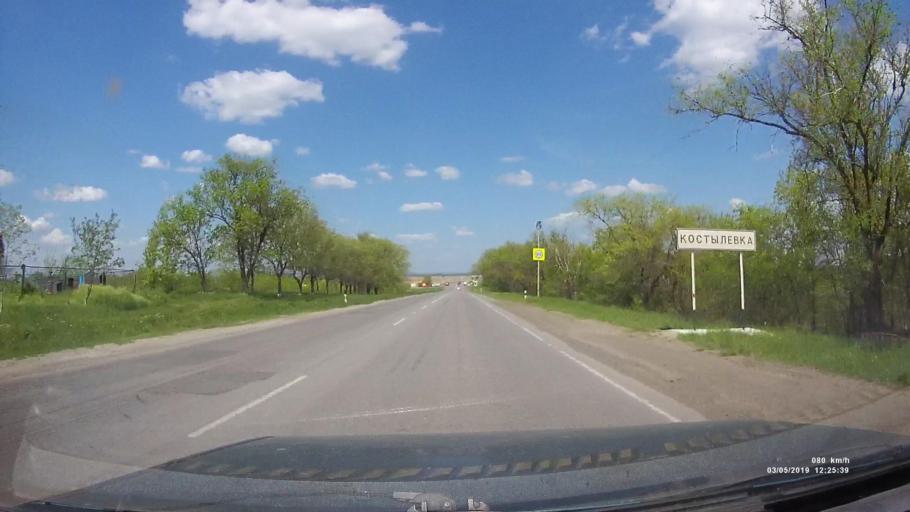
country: RU
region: Rostov
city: Semikarakorsk
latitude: 47.4357
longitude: 40.7117
